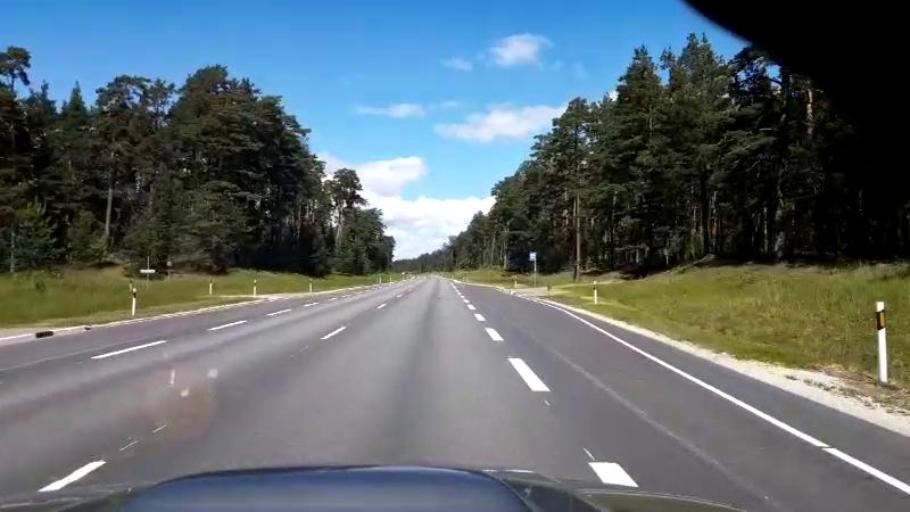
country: EE
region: Paernumaa
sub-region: Paernu linn
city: Parnu
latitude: 58.1866
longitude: 24.4918
